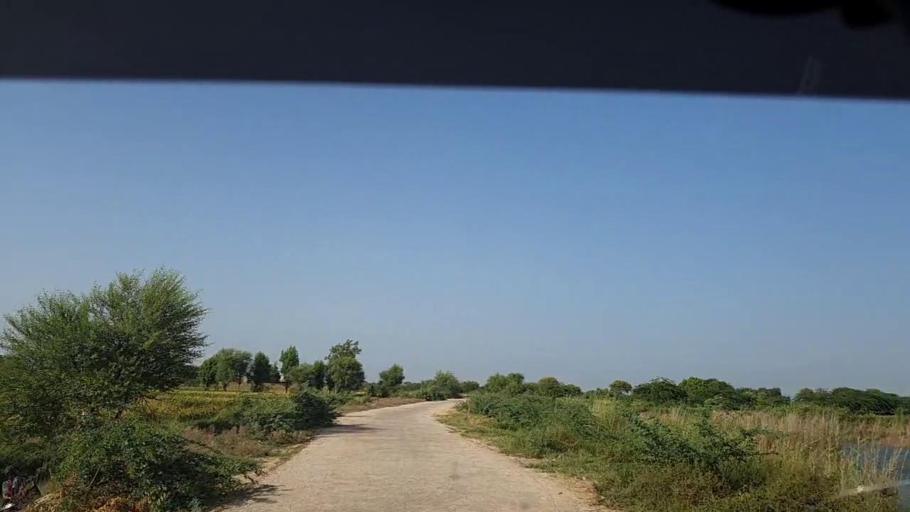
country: PK
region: Sindh
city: Badin
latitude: 24.6834
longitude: 68.8409
